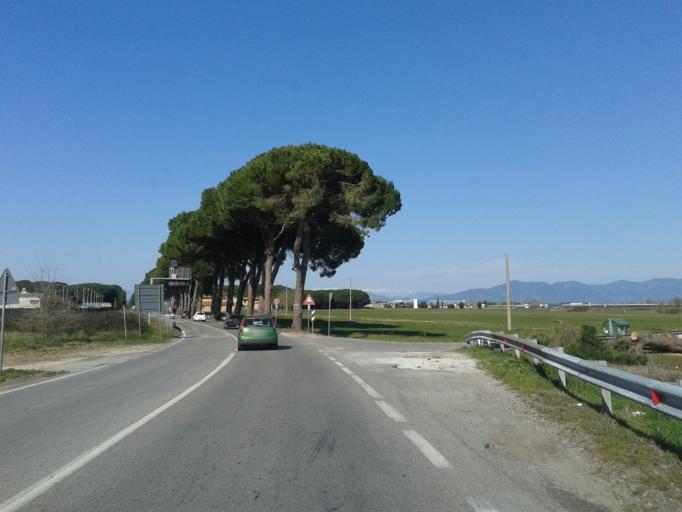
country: IT
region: Tuscany
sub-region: Provincia di Livorno
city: Guasticce
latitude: 43.6042
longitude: 10.3529
